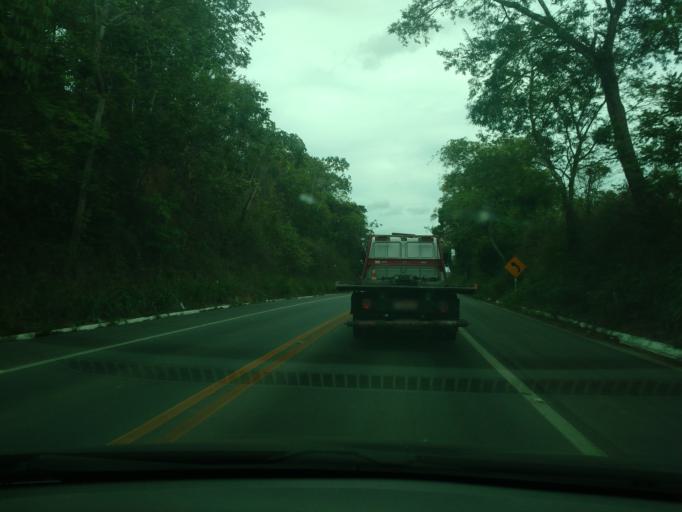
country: BR
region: Alagoas
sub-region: Murici
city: Murici
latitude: -9.3297
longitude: -35.9167
